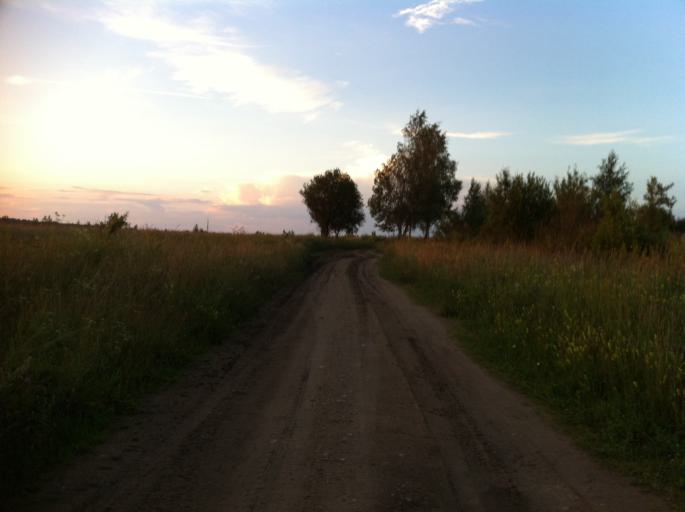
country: RU
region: Pskov
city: Izborsk
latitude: 57.8240
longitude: 27.9683
